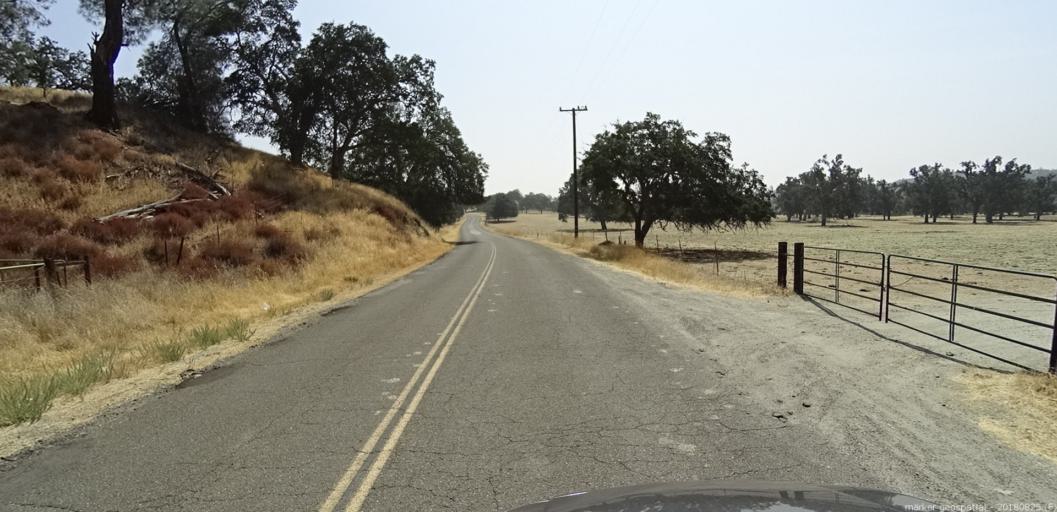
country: US
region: California
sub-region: Fresno County
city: Coalinga
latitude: 35.9133
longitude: -120.4804
